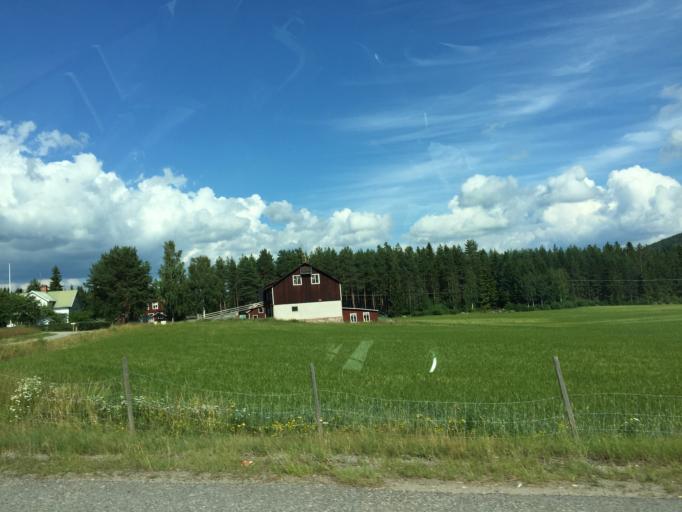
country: SE
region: Gaevleborg
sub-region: Bollnas Kommun
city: Kilafors
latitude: 61.2617
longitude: 16.5522
